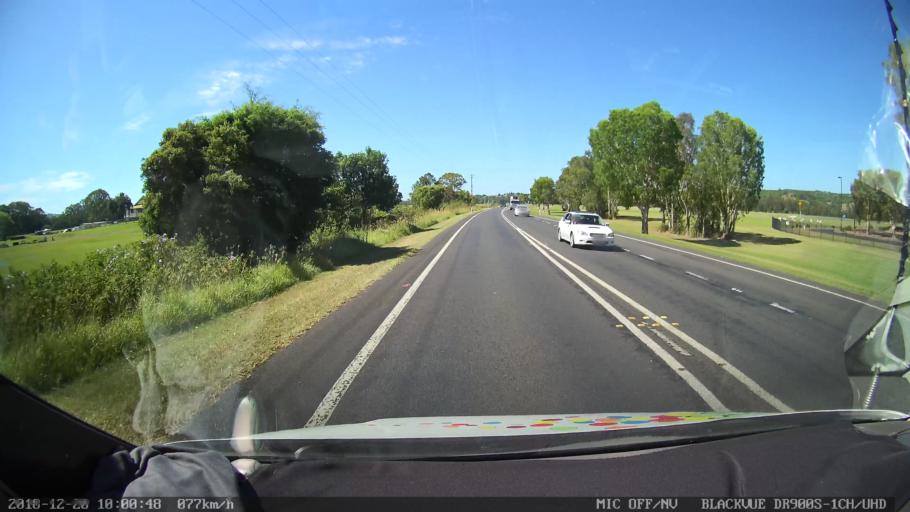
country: AU
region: New South Wales
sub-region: Lismore Municipality
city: Lismore
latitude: -28.8366
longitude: 153.2644
